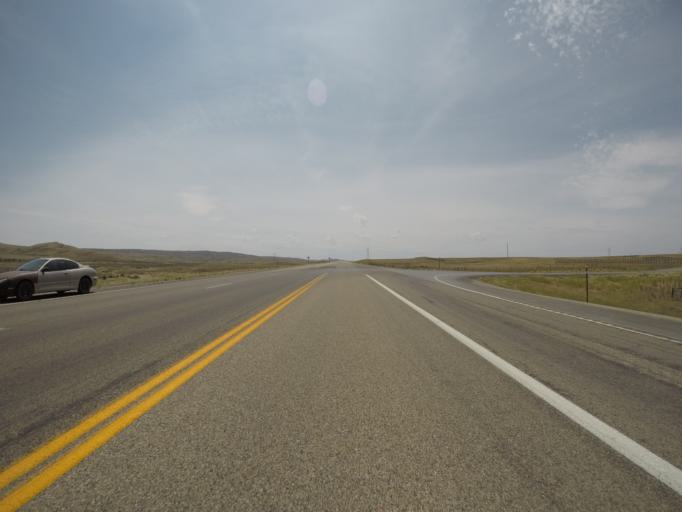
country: US
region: Wyoming
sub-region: Lincoln County
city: Kemmerer
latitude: 41.7490
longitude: -110.5650
